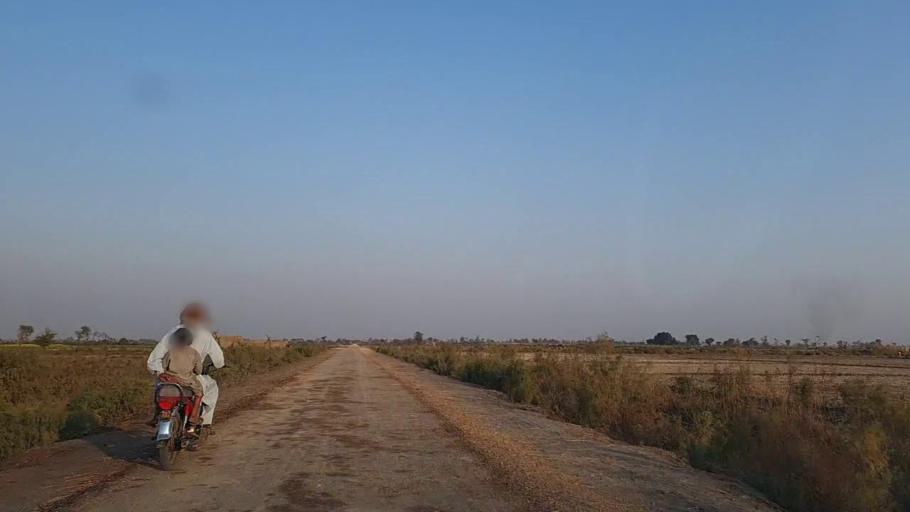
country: PK
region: Sindh
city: Bandhi
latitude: 26.5427
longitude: 68.3121
